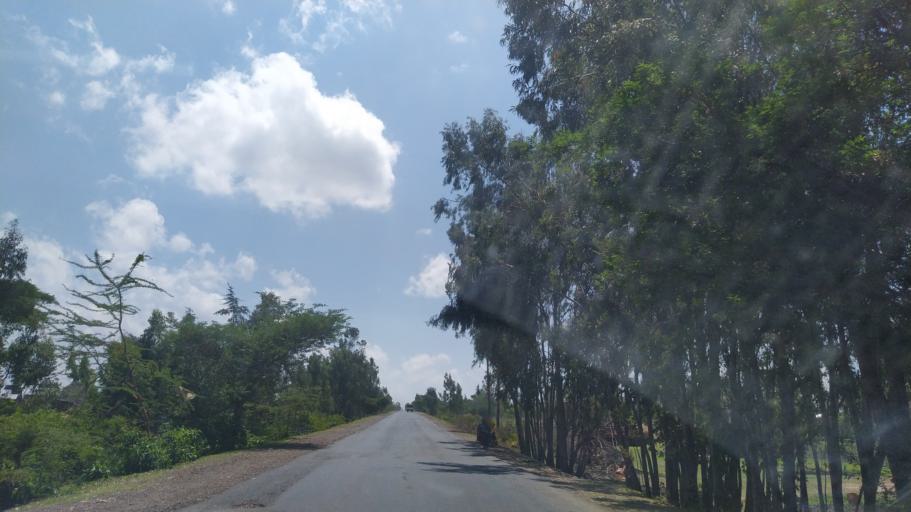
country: ET
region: Southern Nations, Nationalities, and People's Region
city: Butajira
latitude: 7.7563
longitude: 38.1308
